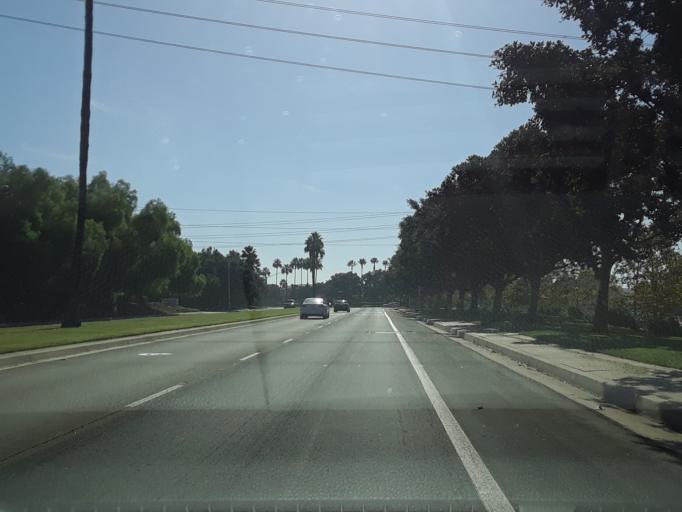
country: US
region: California
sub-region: Orange County
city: Irvine
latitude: 33.6631
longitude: -117.7691
